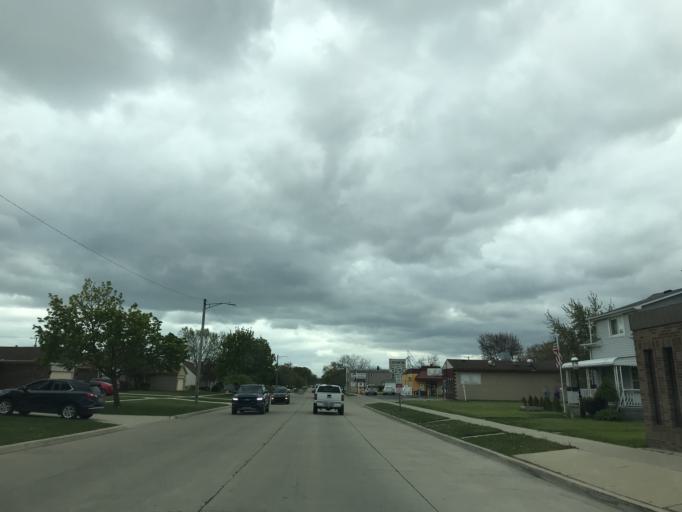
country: US
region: Michigan
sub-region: Wayne County
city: Riverview
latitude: 42.1846
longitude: -83.1796
